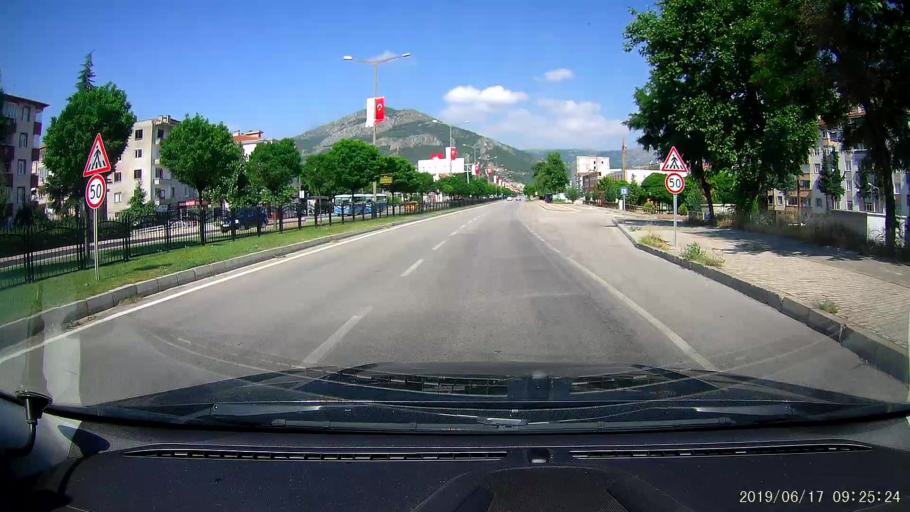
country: TR
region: Amasya
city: Amasya
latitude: 40.6677
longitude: 35.8492
